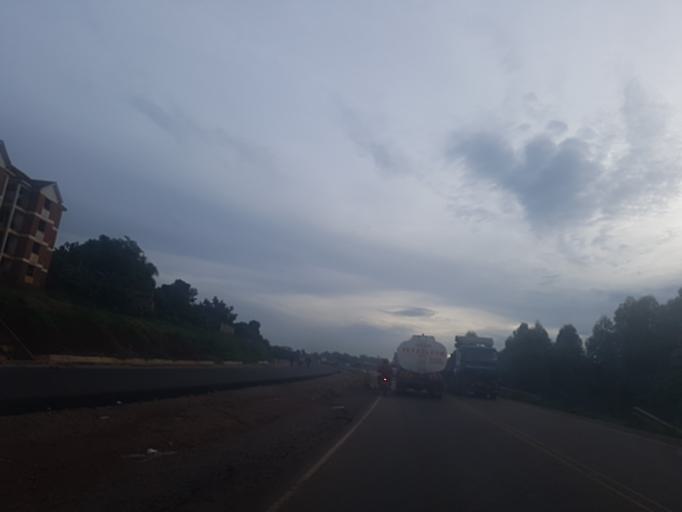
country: UG
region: Central Region
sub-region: Wakiso District
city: Kireka
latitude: 0.3684
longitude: 32.6149
